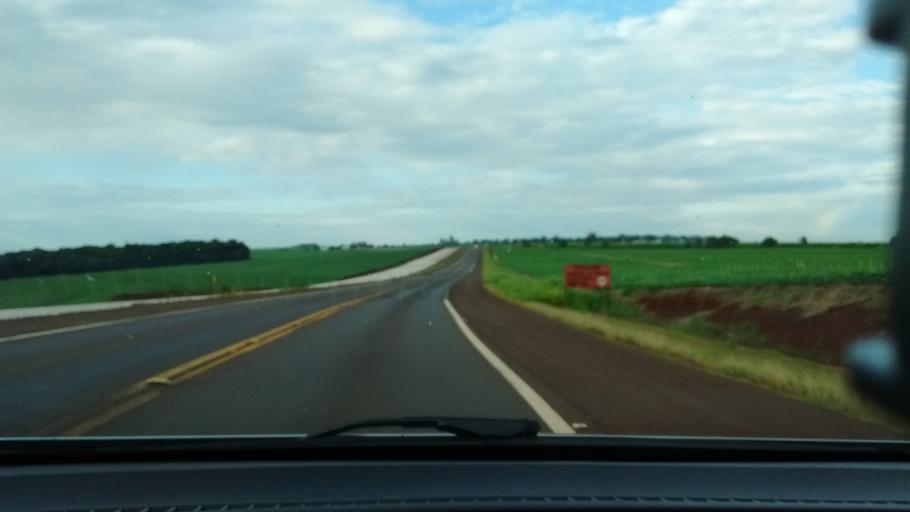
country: BR
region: Parana
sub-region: Cascavel
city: Cascavel
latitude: -25.0323
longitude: -53.5494
